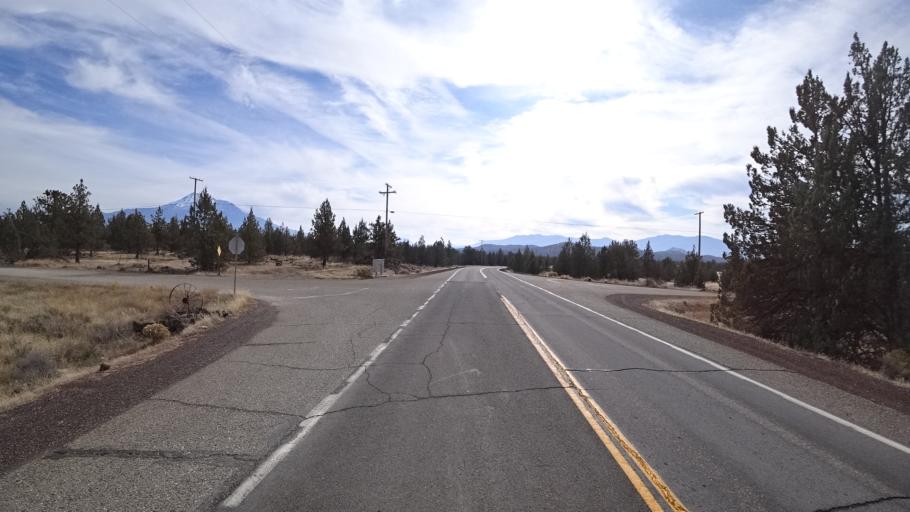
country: US
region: California
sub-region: Siskiyou County
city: Weed
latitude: 41.5959
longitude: -122.3956
